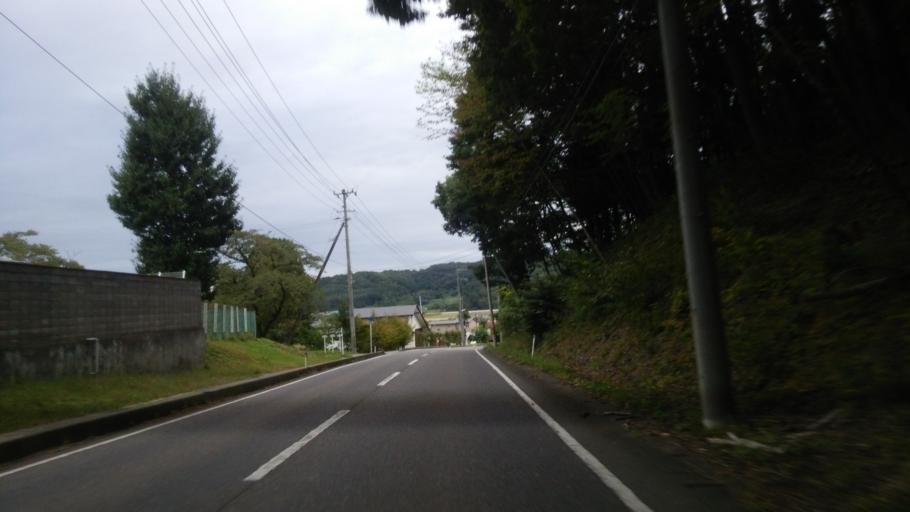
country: JP
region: Fukushima
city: Sukagawa
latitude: 37.2579
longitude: 140.2486
